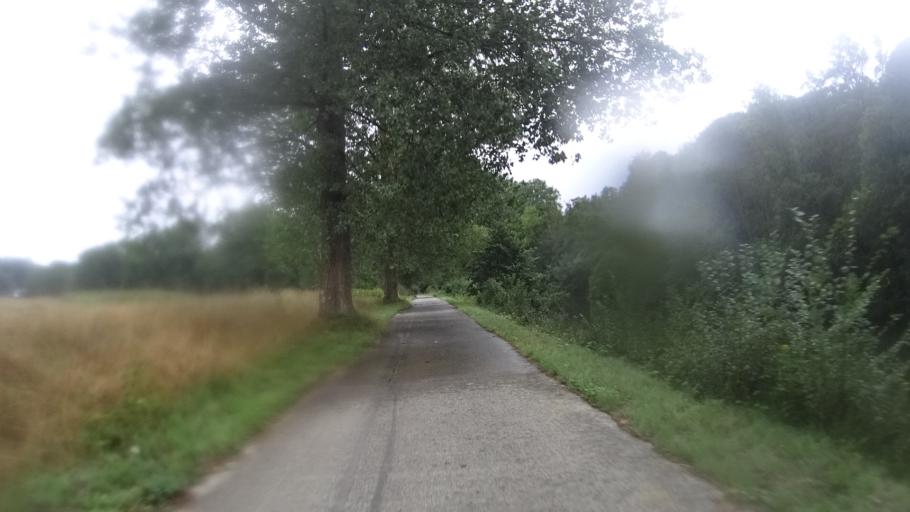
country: BE
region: Wallonia
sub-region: Province du Hainaut
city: Lobbes
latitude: 50.3427
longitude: 4.2482
